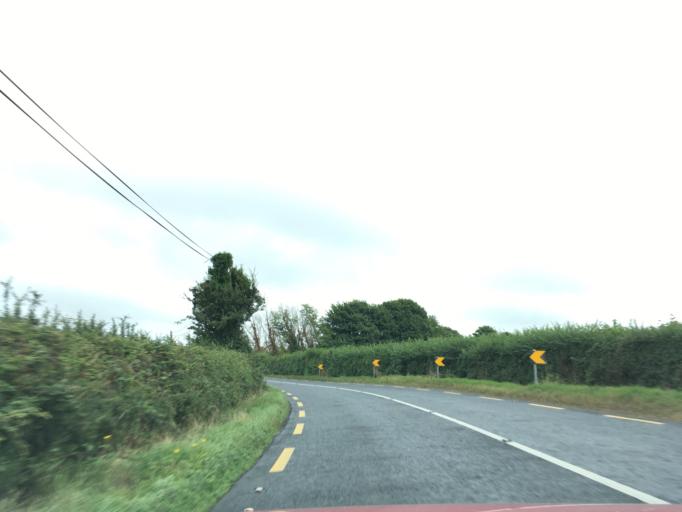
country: IE
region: Munster
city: Fethard
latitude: 52.4204
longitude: -7.7681
